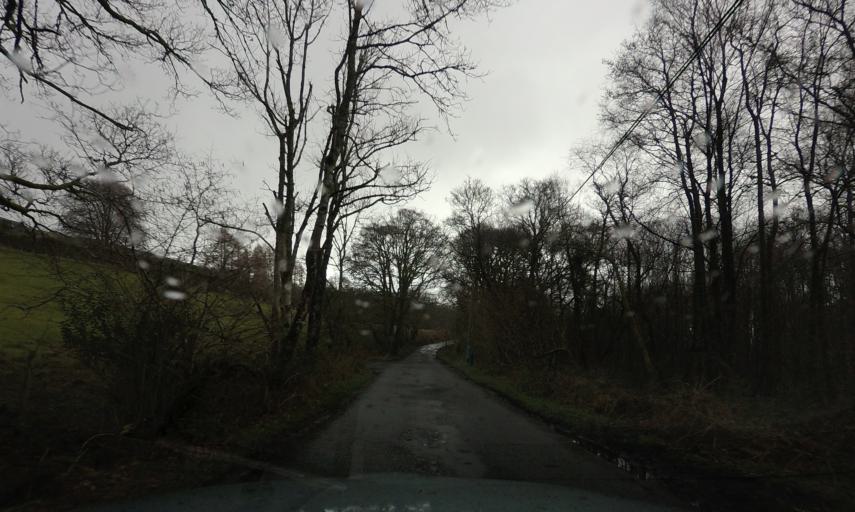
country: GB
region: Scotland
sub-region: West Dunbartonshire
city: Balloch
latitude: 56.1377
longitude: -4.6158
